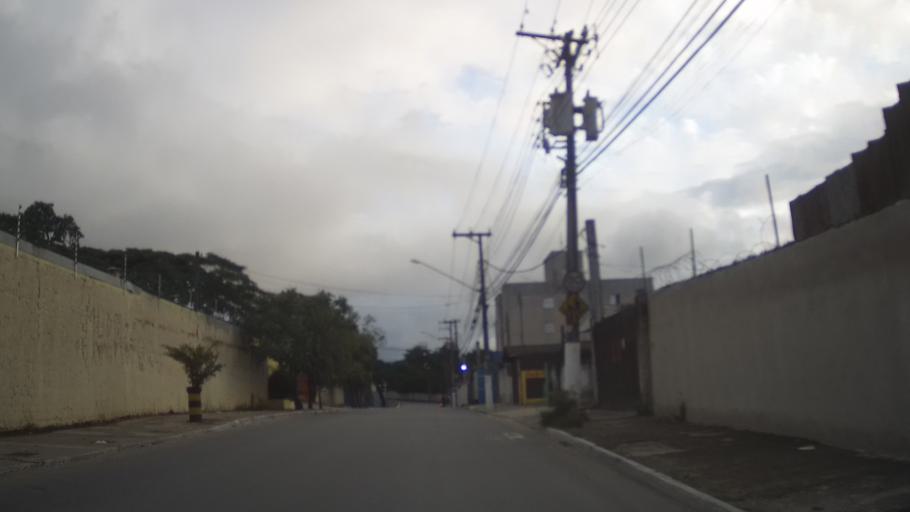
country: BR
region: Sao Paulo
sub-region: Itaquaquecetuba
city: Itaquaquecetuba
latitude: -23.4441
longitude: -46.4270
